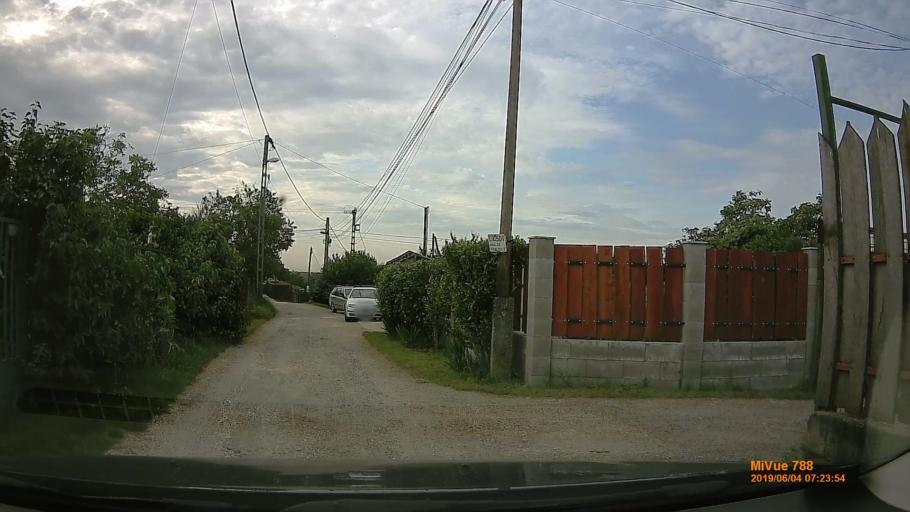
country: HU
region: Pest
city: Diosd
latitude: 47.4021
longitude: 18.9654
